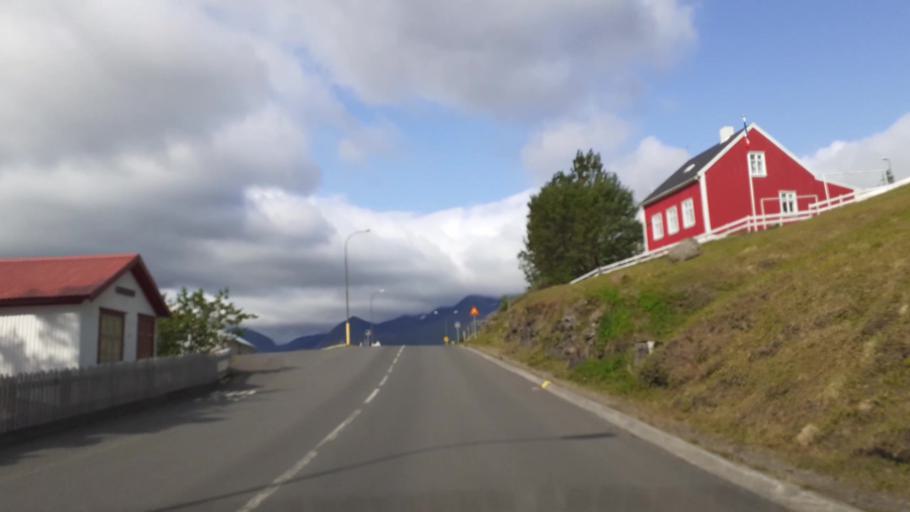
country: IS
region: East
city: Eskifjoerdur
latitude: 64.9268
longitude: -14.0020
